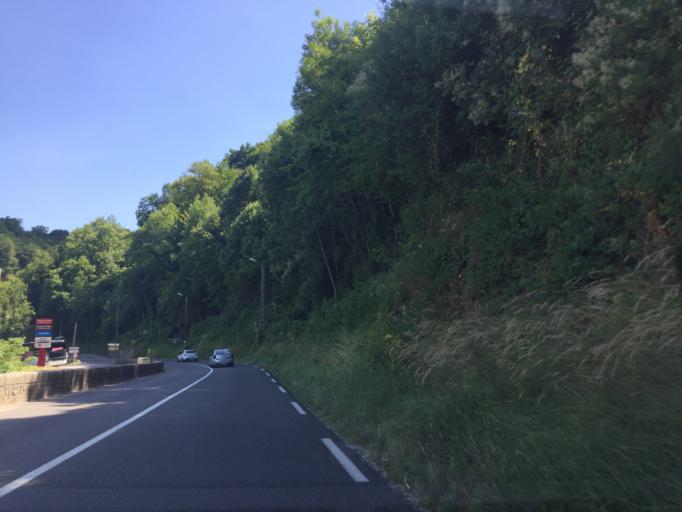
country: FR
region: Rhone-Alpes
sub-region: Departement de l'Isere
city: Saint-Hilaire-du-Rosier
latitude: 45.0615
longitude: 5.2426
